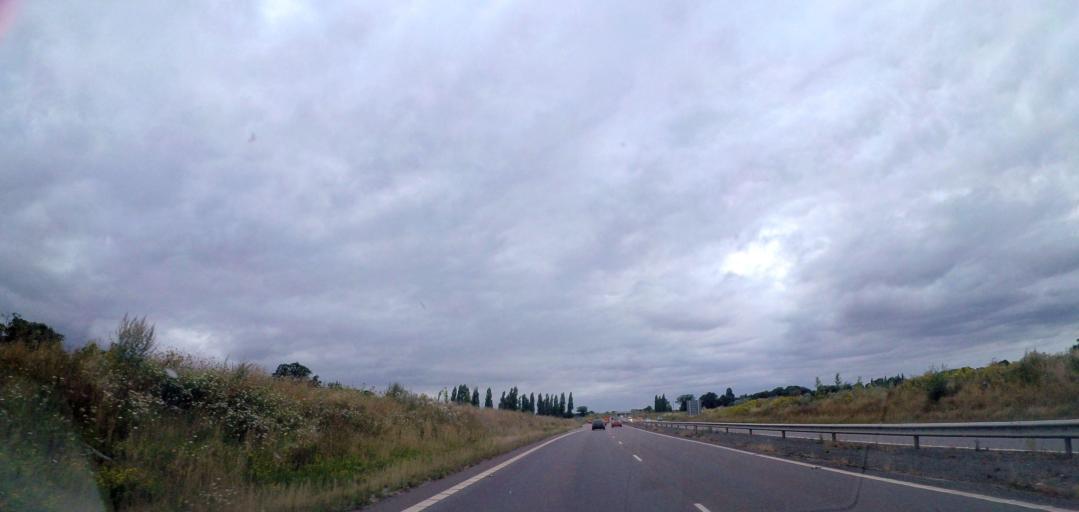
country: GB
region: England
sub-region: Norfolk
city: Surlingham
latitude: 52.6360
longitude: 1.3835
